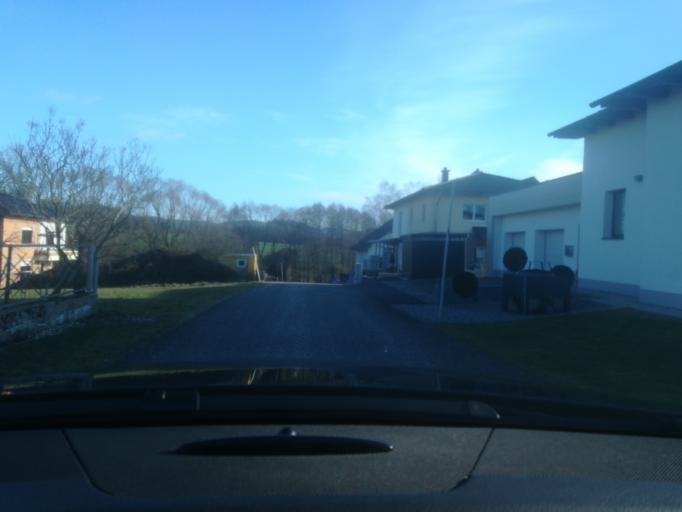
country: AT
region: Upper Austria
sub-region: Politischer Bezirk Urfahr-Umgebung
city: Herzogsdorf
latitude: 48.4359
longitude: 14.1176
